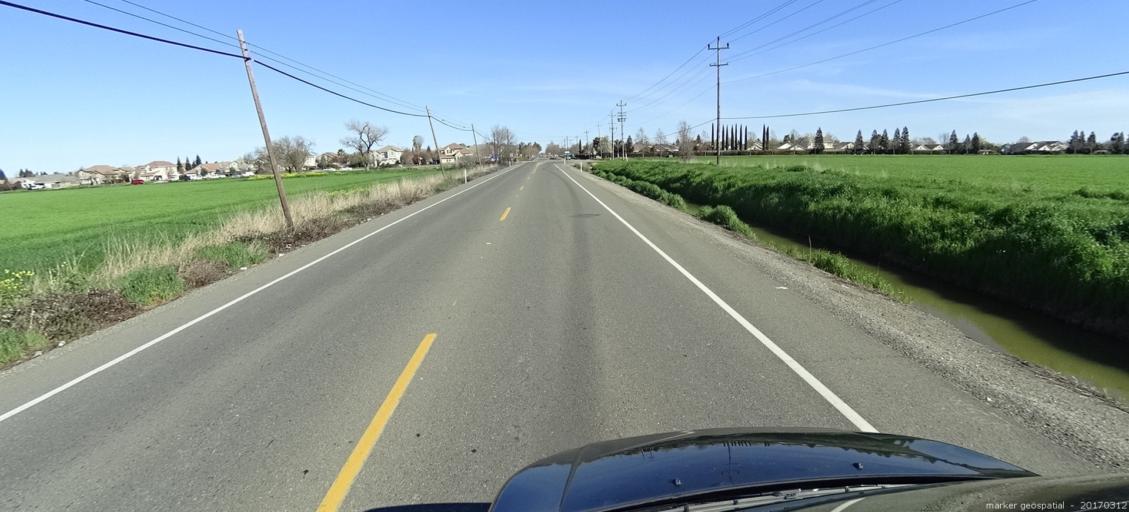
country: US
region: California
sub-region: Yolo County
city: West Sacramento
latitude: 38.6254
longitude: -121.5396
